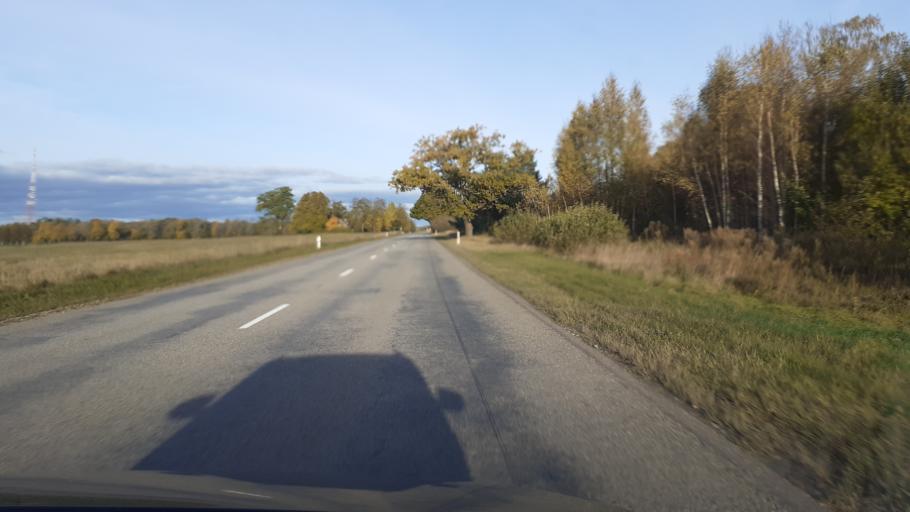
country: LV
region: Kuldigas Rajons
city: Kuldiga
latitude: 56.9316
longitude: 22.0421
